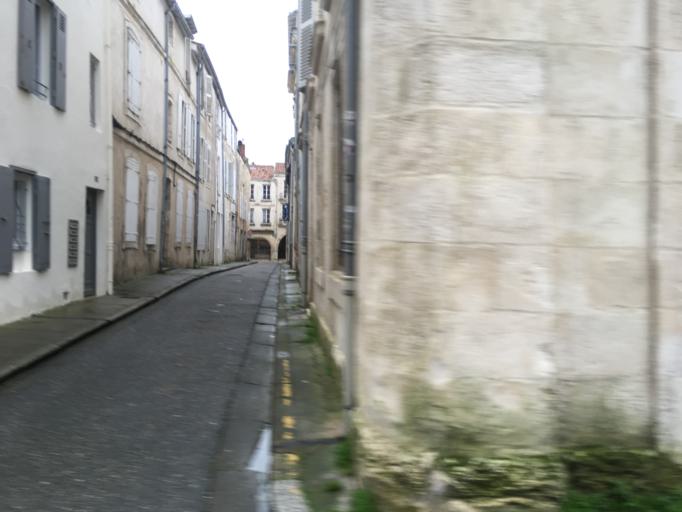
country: FR
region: Poitou-Charentes
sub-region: Departement de la Charente-Maritime
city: La Rochelle
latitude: 46.1634
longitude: -1.1506
